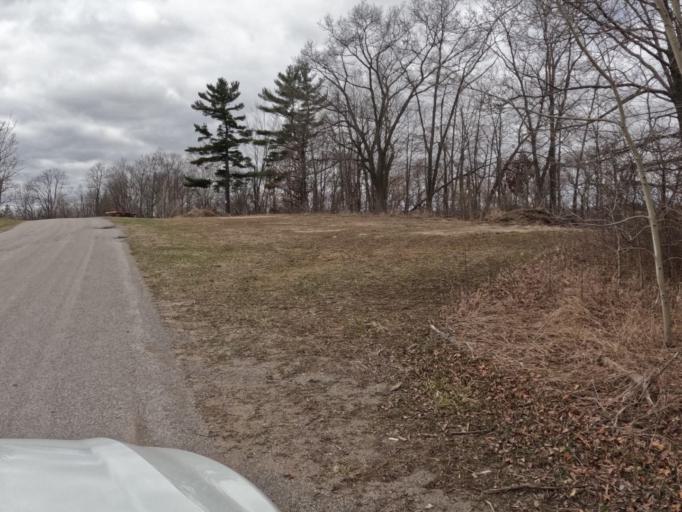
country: CA
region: Ontario
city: Norfolk County
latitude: 42.8213
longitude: -80.4942
